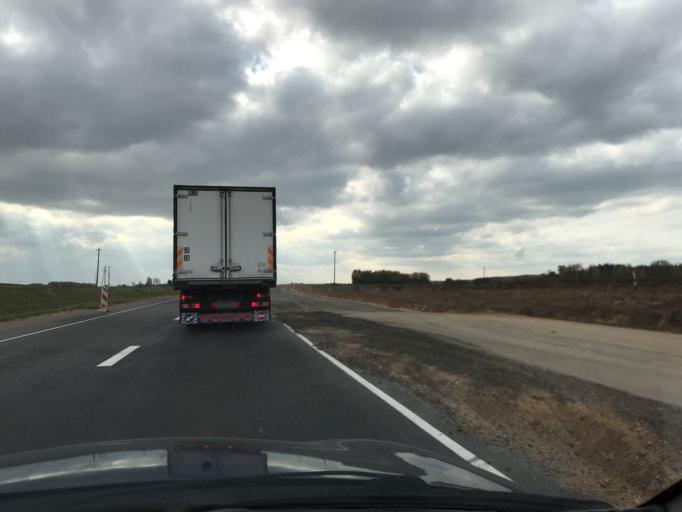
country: BY
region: Grodnenskaya
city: Lida
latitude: 53.8165
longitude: 25.1189
